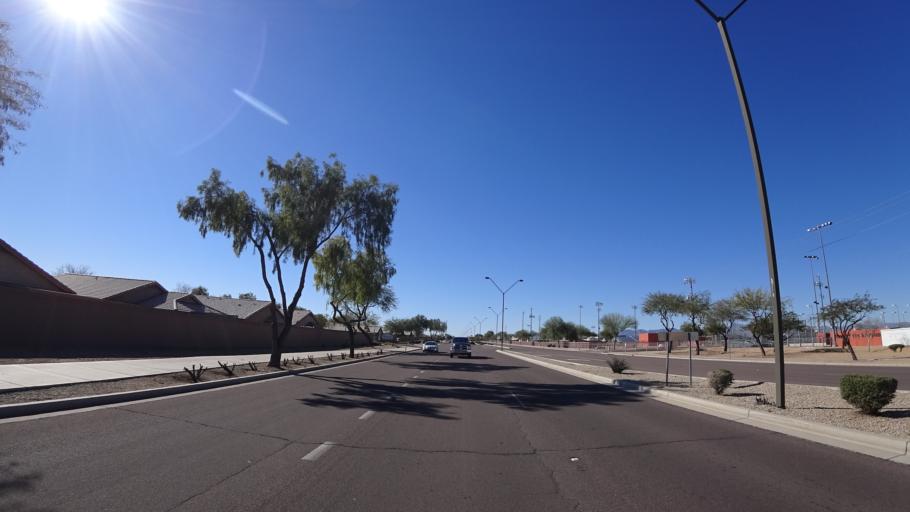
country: US
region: Arizona
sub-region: Maricopa County
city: Goodyear
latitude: 33.4355
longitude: -112.3990
